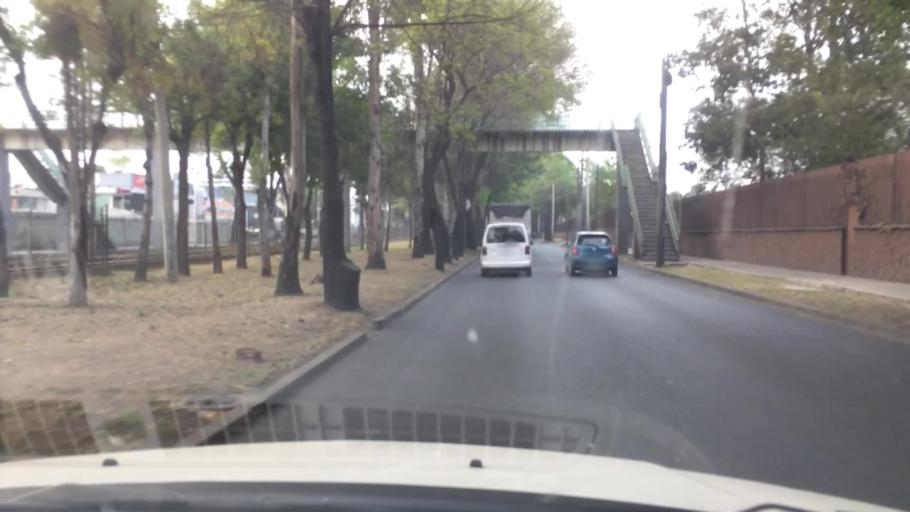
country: MX
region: Mexico City
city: Tlalpan
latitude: 19.2843
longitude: -99.1413
